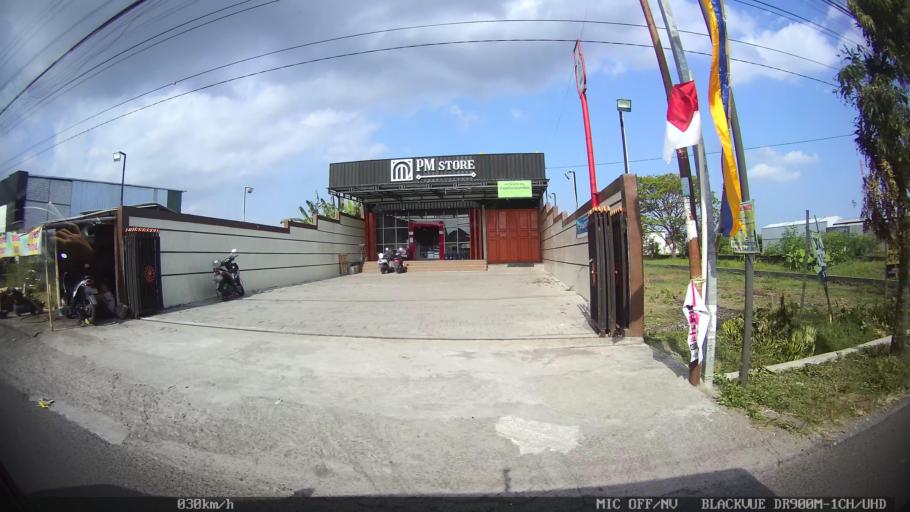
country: ID
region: Daerah Istimewa Yogyakarta
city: Yogyakarta
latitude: -7.7946
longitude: 110.3460
